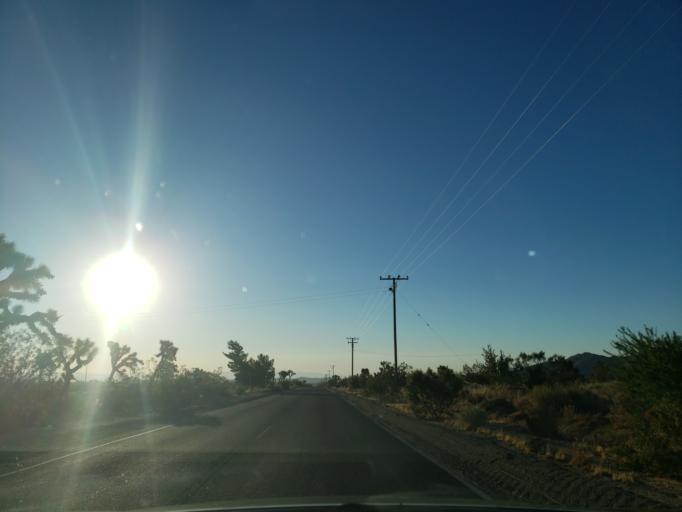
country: US
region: California
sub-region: San Bernardino County
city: Joshua Tree
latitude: 34.1930
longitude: -116.3767
